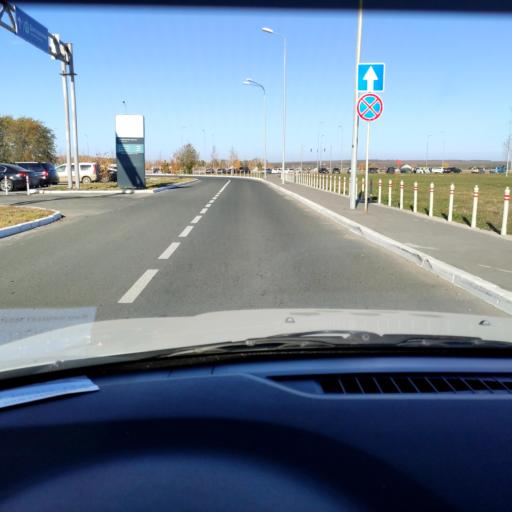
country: RU
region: Samara
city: Bereza
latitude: 53.5137
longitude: 50.1547
